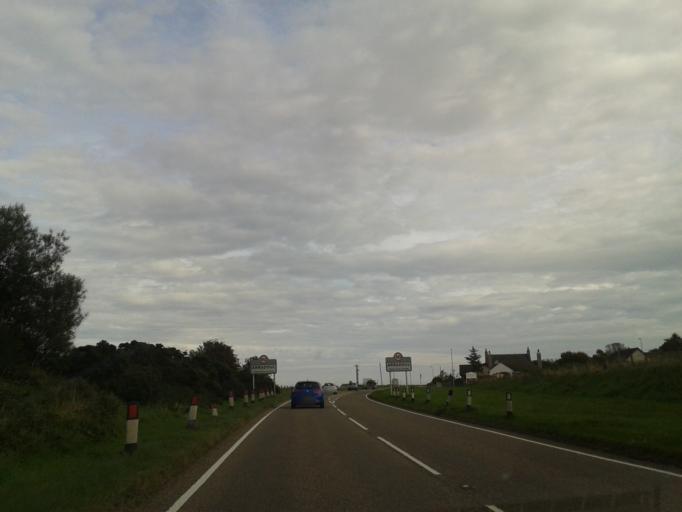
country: GB
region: Scotland
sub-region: Moray
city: Buckie
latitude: 57.6569
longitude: -2.9842
